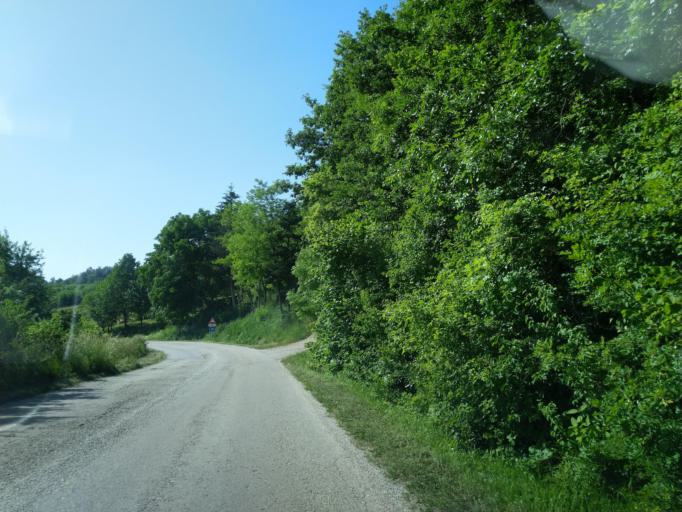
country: RS
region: Central Serbia
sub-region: Zlatiborski Okrug
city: Cajetina
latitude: 43.8702
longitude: 19.6960
